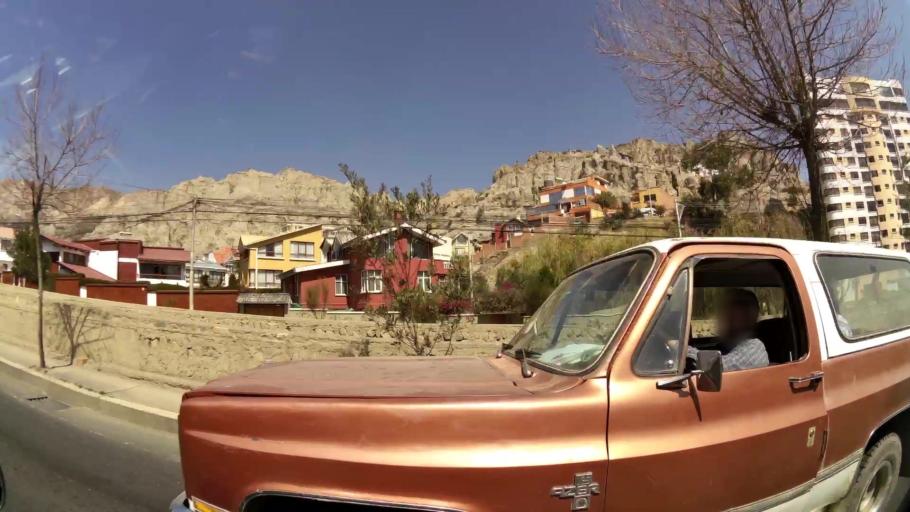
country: BO
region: La Paz
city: La Paz
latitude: -16.5462
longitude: -68.0797
